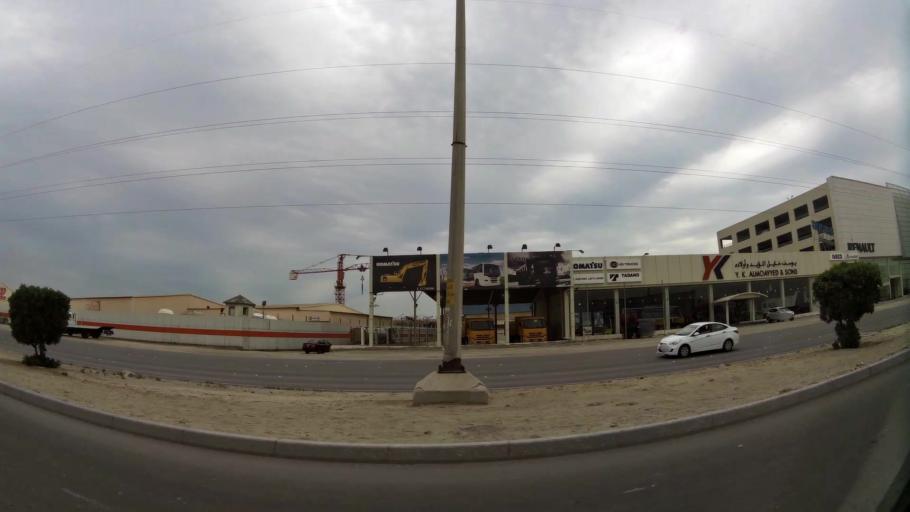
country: BH
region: Northern
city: Sitrah
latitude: 26.1522
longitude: 50.6162
